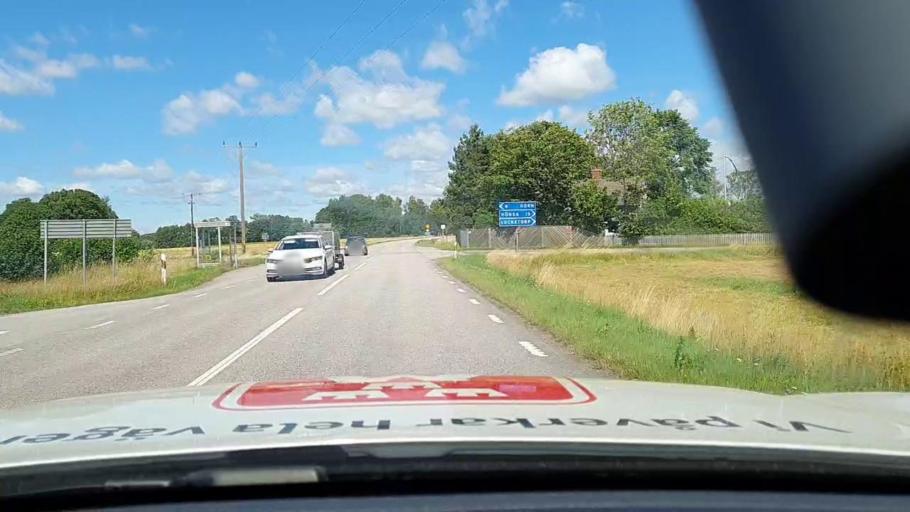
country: SE
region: Vaestra Goetaland
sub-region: Skovde Kommun
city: Stopen
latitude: 58.4874
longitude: 13.9601
